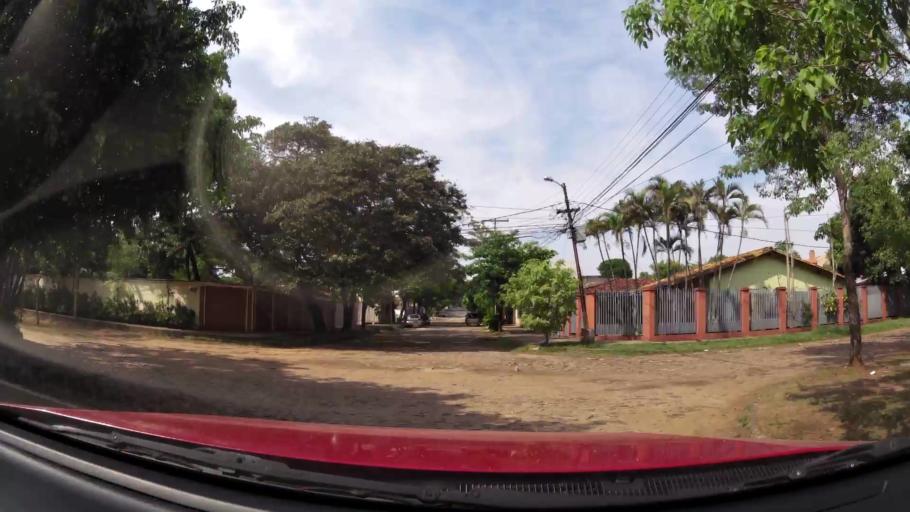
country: PY
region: Asuncion
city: Asuncion
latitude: -25.2639
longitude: -57.5646
